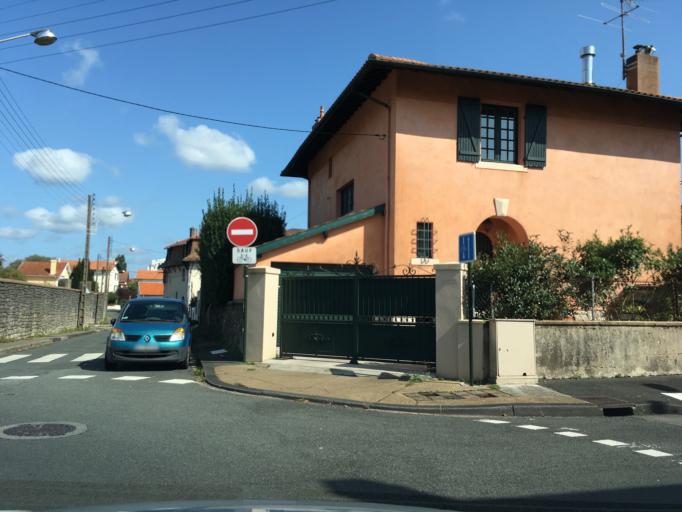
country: FR
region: Aquitaine
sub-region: Departement des Pyrenees-Atlantiques
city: Bayonne
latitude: 43.4837
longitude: -1.4853
